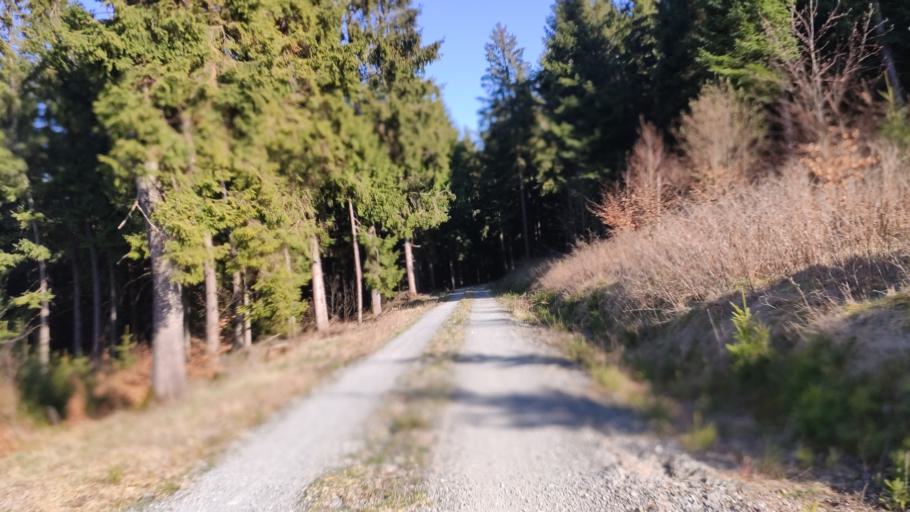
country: DE
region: Bavaria
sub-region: Upper Franconia
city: Reichenbach
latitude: 50.4450
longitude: 11.4347
